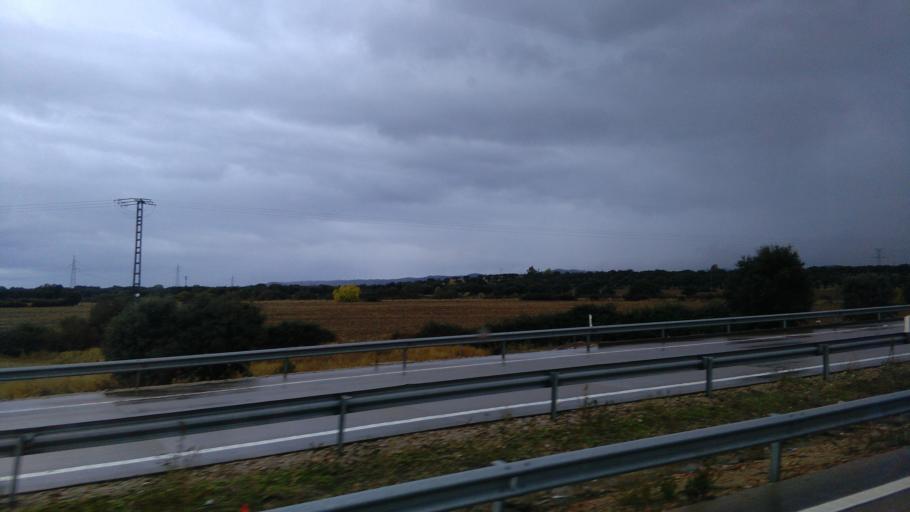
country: ES
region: Castille-La Mancha
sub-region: Province of Toledo
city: Cervera de los Montes
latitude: 40.0030
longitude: -4.7684
